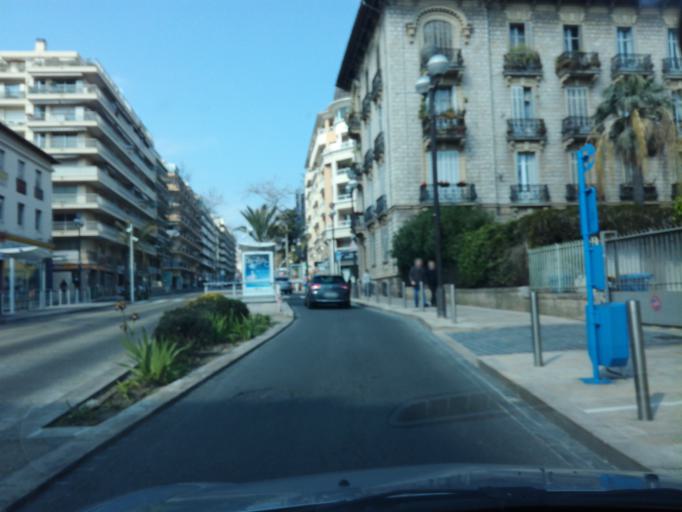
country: FR
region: Provence-Alpes-Cote d'Azur
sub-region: Departement des Alpes-Maritimes
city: Cannes
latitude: 43.5604
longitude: 7.0169
